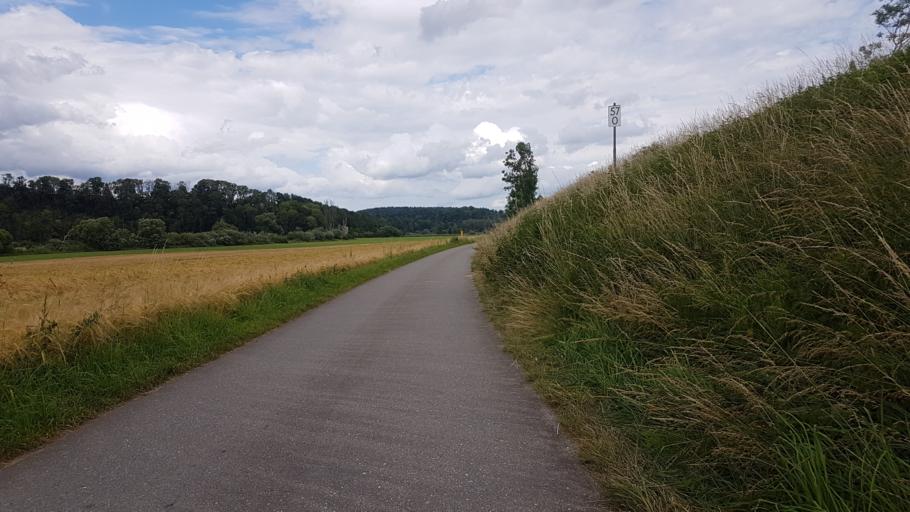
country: DE
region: Baden-Wuerttemberg
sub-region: Tuebingen Region
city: Emeringen
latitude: 48.2148
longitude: 9.5212
